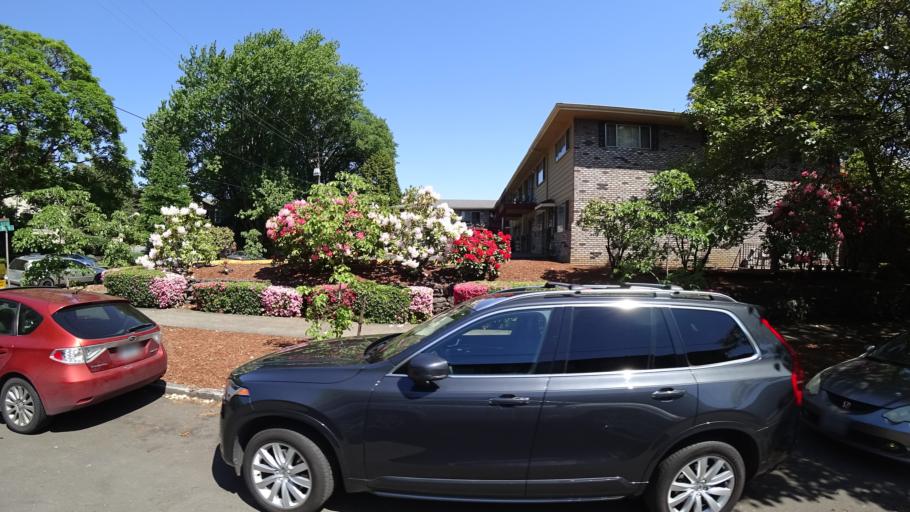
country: US
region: Oregon
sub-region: Multnomah County
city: Portland
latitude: 45.5321
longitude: -122.6467
